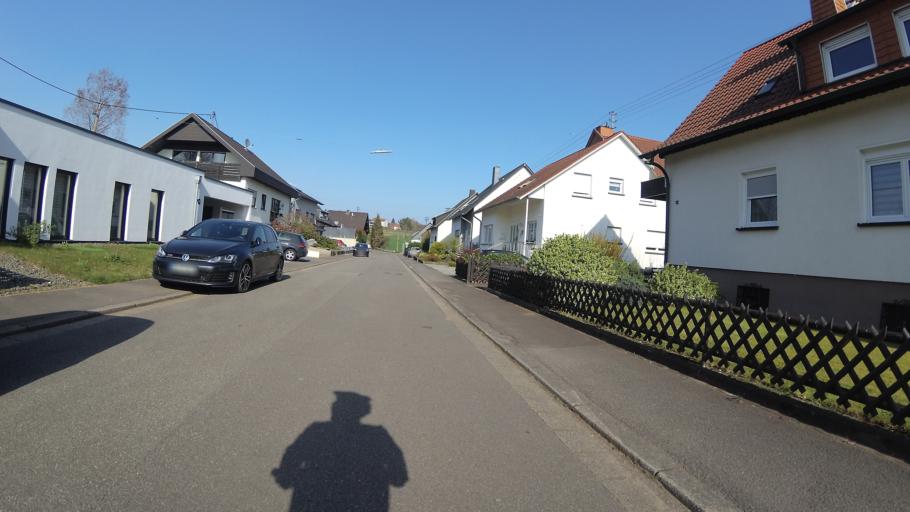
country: DE
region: Saarland
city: Heusweiler
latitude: 49.3342
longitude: 6.9355
